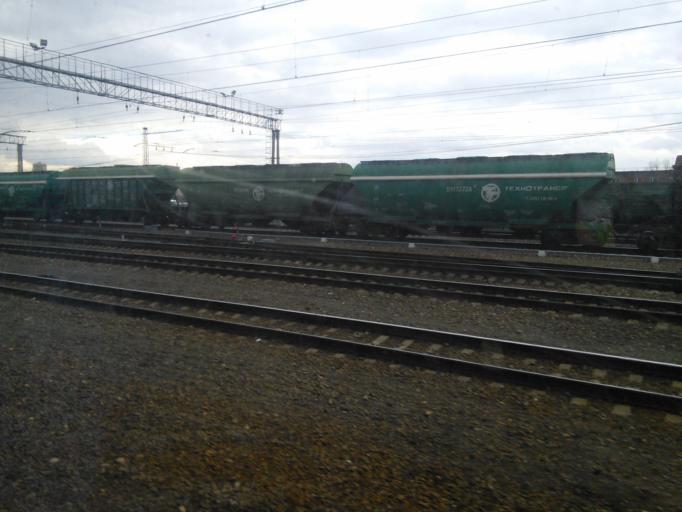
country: RU
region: Moskovskaya
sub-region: Podol'skiy Rayon
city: Podol'sk
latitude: 55.4361
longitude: 37.5674
